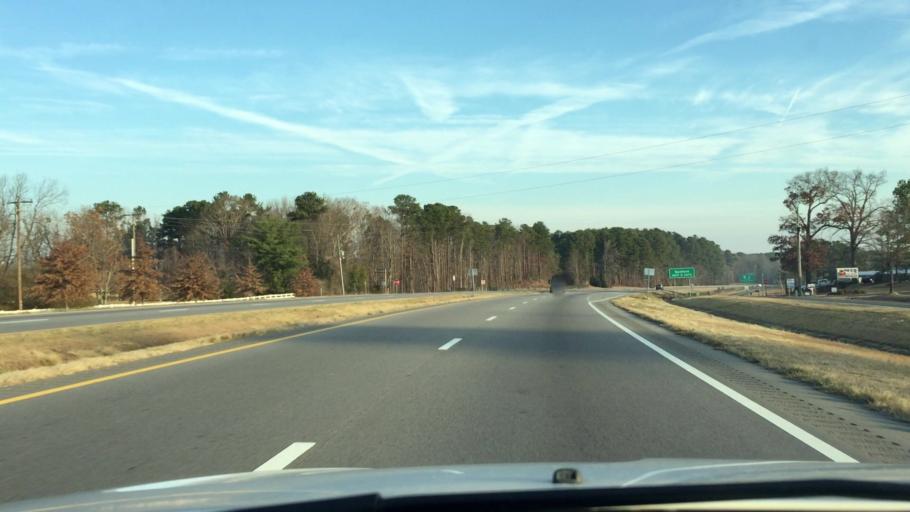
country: US
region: North Carolina
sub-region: Lee County
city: Sanford
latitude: 35.4494
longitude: -79.2147
